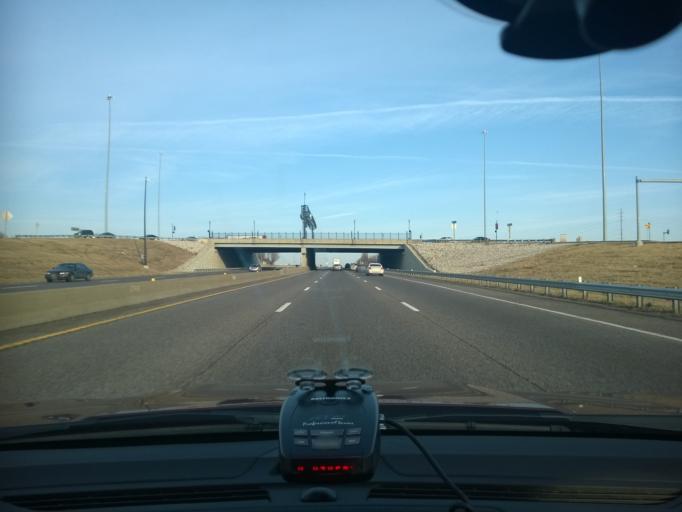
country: US
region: Missouri
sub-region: Saint Charles County
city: Saint Charles
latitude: 38.7761
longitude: -90.5107
